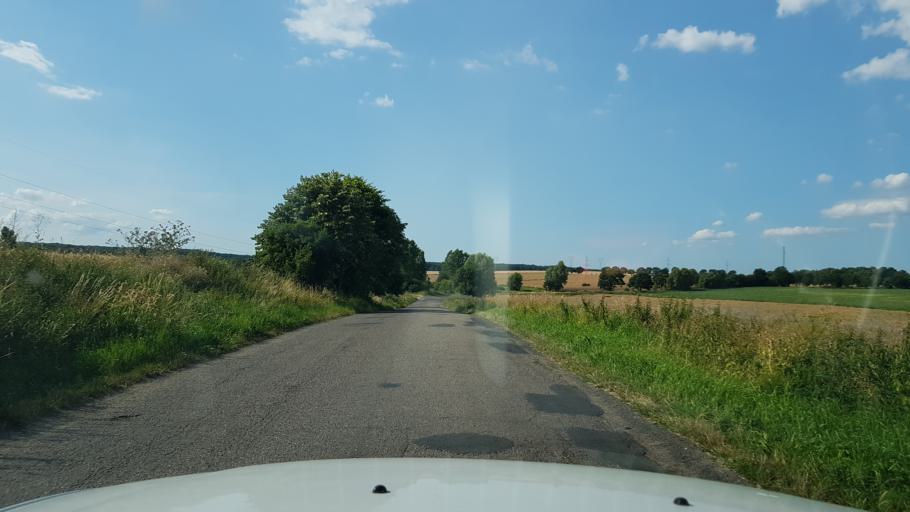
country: PL
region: West Pomeranian Voivodeship
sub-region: Powiat gryfinski
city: Stare Czarnowo
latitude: 53.2937
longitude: 14.8052
